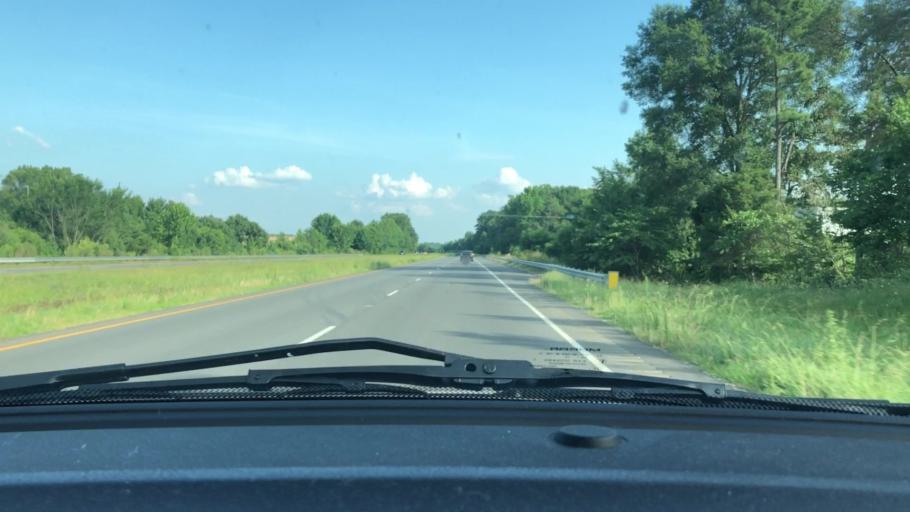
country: US
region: North Carolina
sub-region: Chatham County
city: Siler City
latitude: 35.6745
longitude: -79.4132
